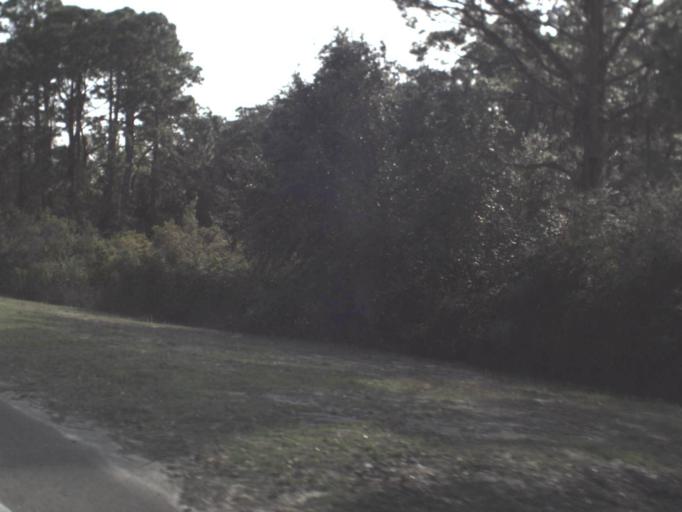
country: US
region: Florida
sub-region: Bay County
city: Tyndall Air Force Base
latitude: 30.0970
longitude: -85.6126
